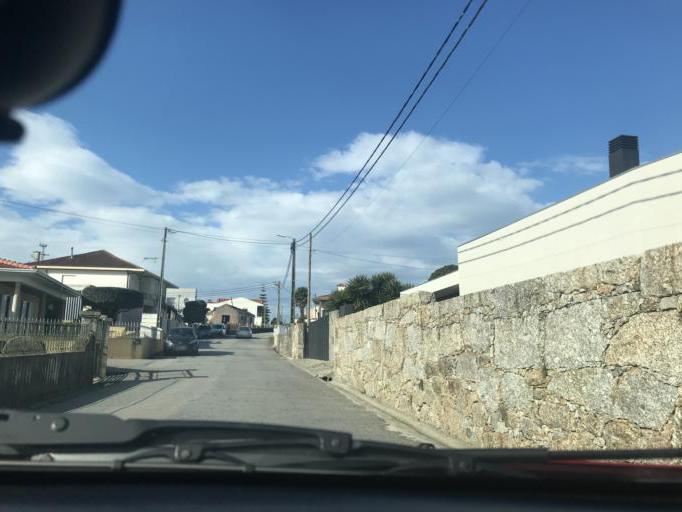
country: PT
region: Braga
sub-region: Vila Nova de Famalicao
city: Vila Nova de Famalicao
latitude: 41.4171
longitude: -8.5100
